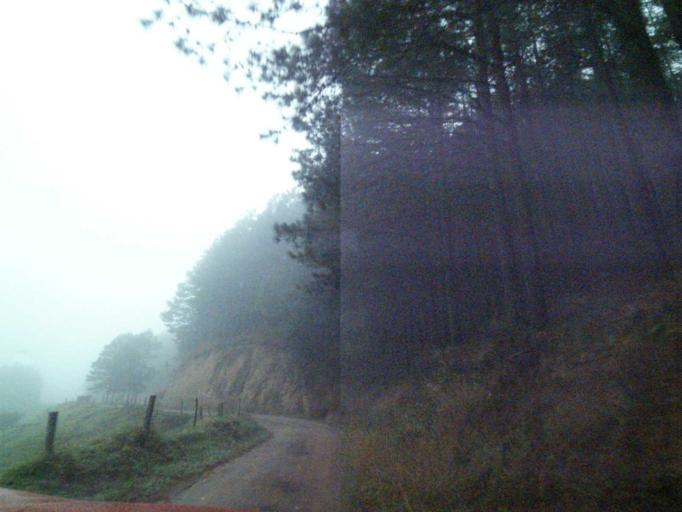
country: BR
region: Santa Catarina
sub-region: Anitapolis
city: Anitapolis
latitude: -27.9131
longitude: -49.0993
